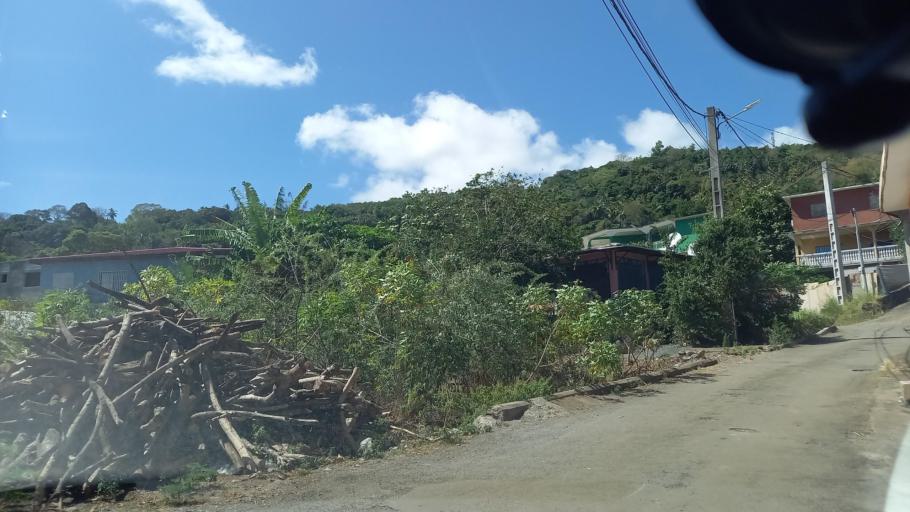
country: YT
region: Kani-Keli
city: Kani Keli
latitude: -12.9656
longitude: 45.1118
